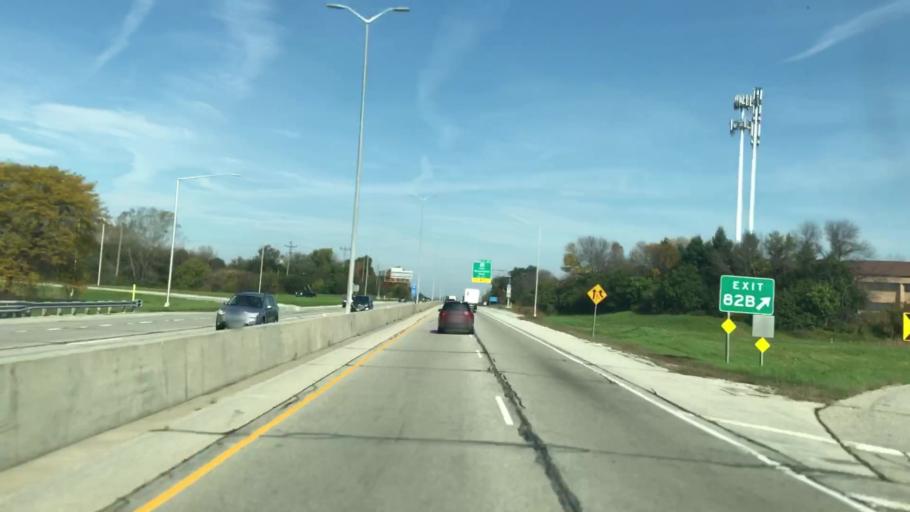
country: US
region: Wisconsin
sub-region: Milwaukee County
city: River Hills
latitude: 43.1776
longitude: -87.9176
